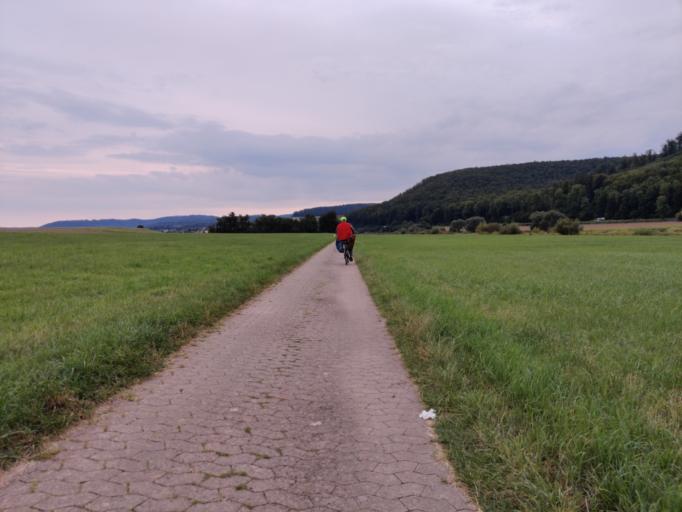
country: DE
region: Lower Saxony
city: Hehlen
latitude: 51.9921
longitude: 9.4390
